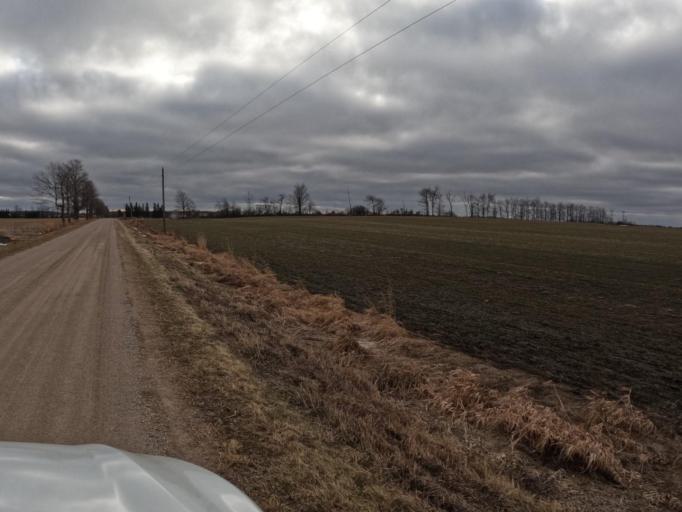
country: CA
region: Ontario
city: Shelburne
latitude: 43.8943
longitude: -80.3298
